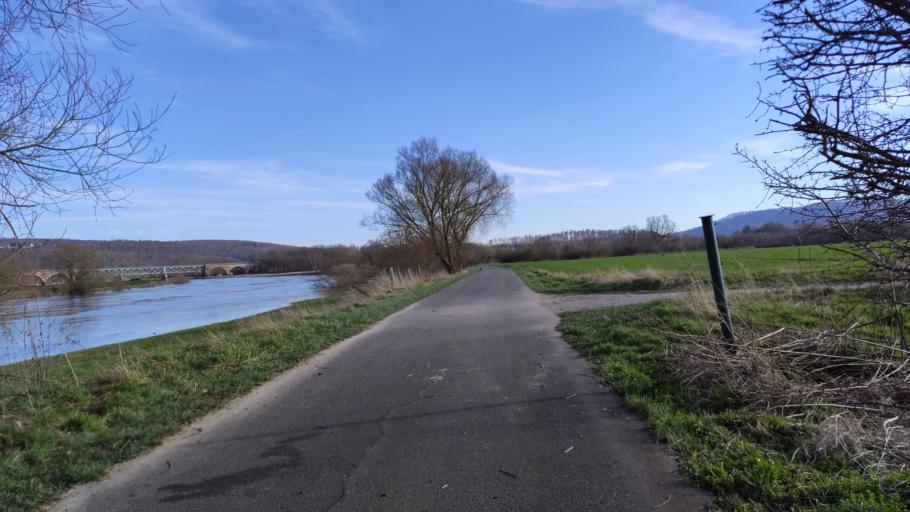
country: DE
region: Lower Saxony
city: Boffzen
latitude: 51.7415
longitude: 9.3747
